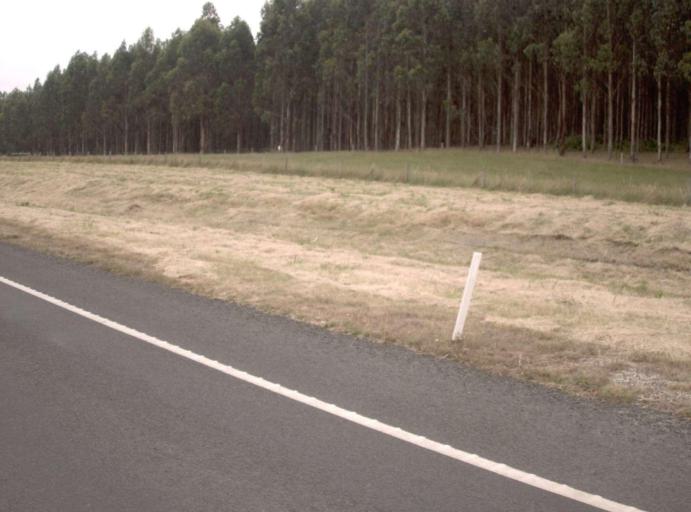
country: AU
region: Victoria
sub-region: Latrobe
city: Morwell
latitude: -38.2426
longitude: 146.3372
